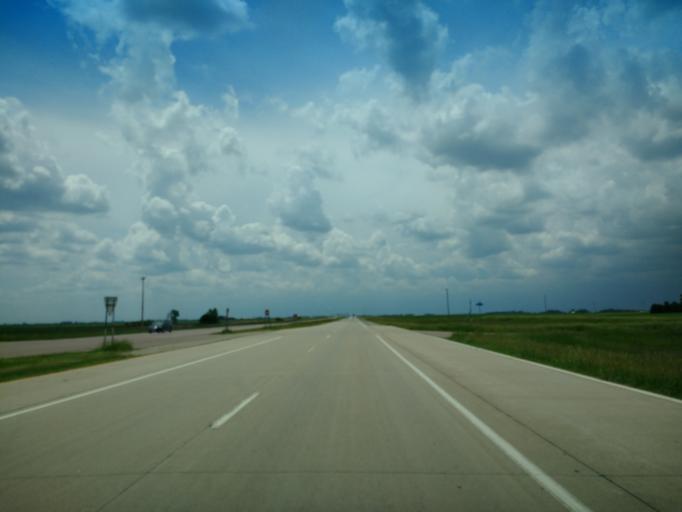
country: US
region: Minnesota
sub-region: Jackson County
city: Lakefield
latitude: 43.7475
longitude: -95.3966
